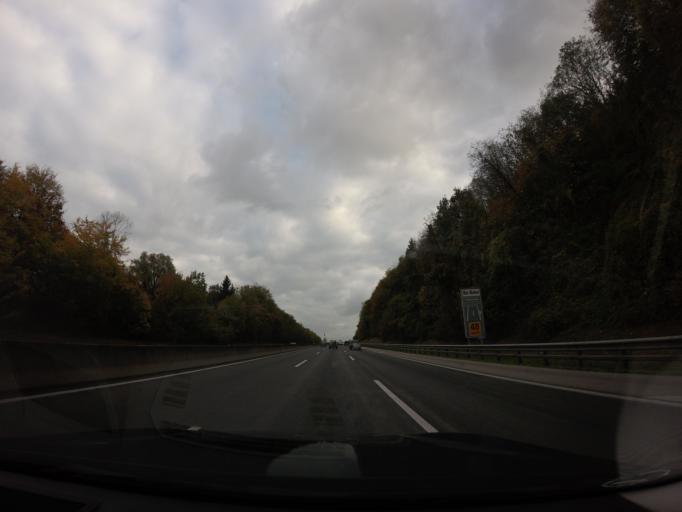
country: AT
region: Lower Austria
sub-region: Politischer Bezirk Amstetten
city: Sankt Valentin
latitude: 48.1599
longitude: 14.5555
